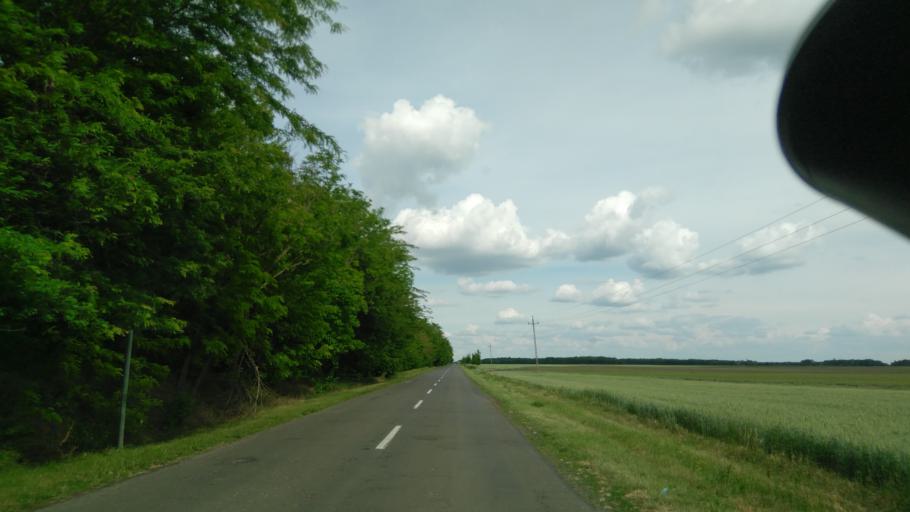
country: RO
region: Arad
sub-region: Comuna Peregu Mare
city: Peregu Mic
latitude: 46.3043
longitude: 20.9076
